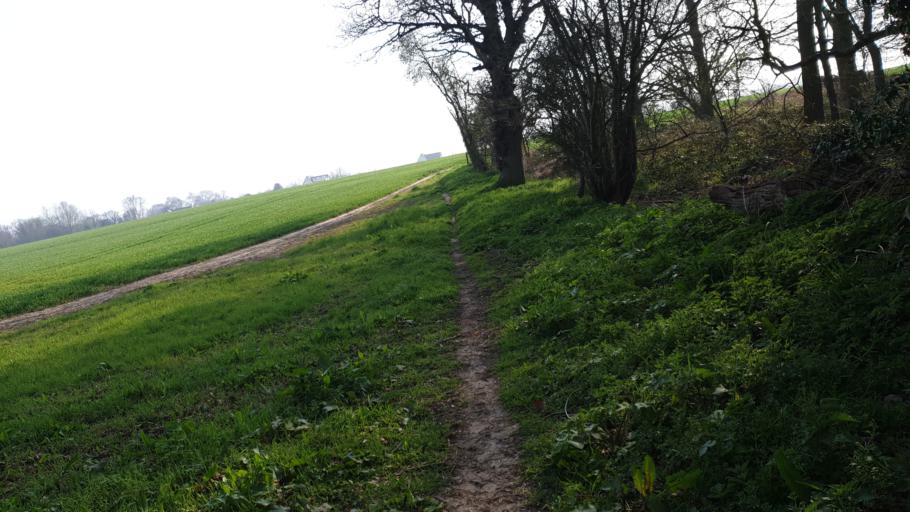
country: GB
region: England
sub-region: Essex
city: Great Bentley
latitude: 51.8847
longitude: 1.1190
